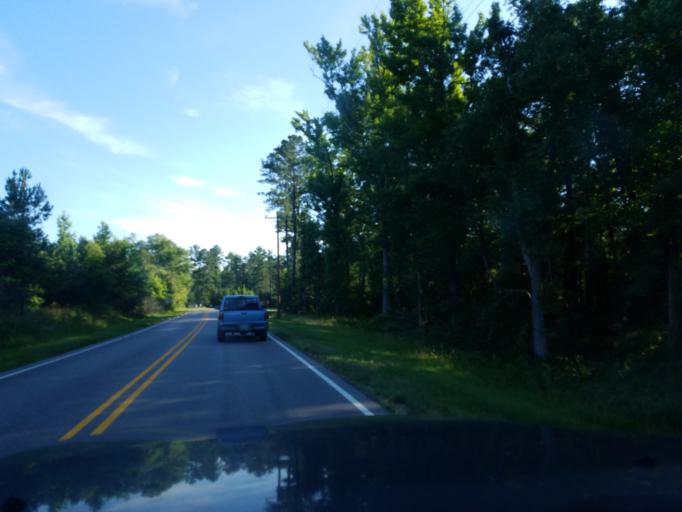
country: US
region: North Carolina
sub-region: Granville County
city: Butner
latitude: 36.1573
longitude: -78.7654
